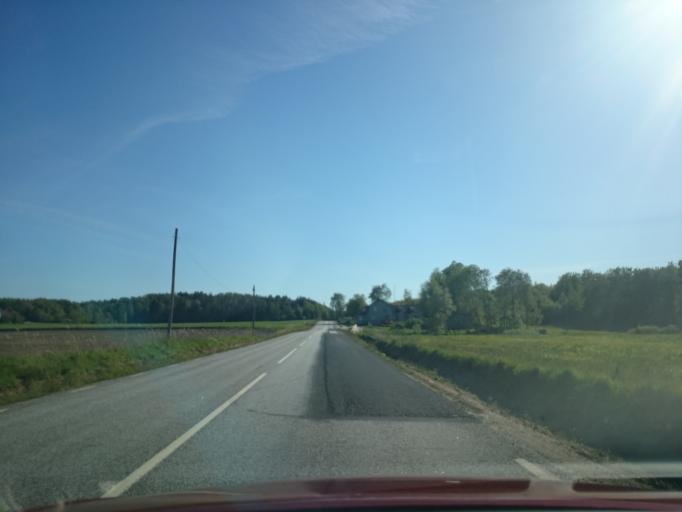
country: SE
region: Vaestra Goetaland
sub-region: Lysekils Kommun
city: Brastad
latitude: 58.2903
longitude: 11.5518
